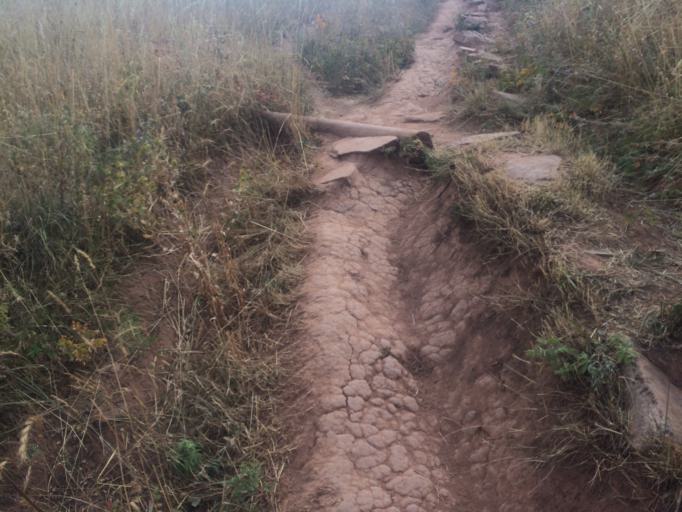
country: US
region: Colorado
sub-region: Boulder County
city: Boulder
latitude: 39.9789
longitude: -105.2839
